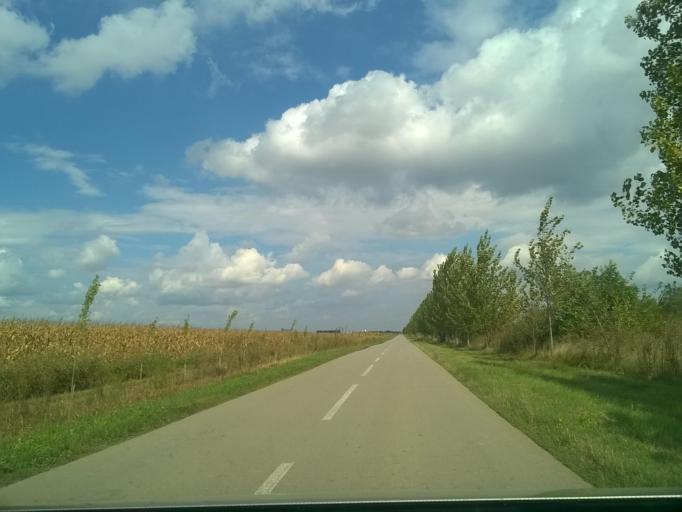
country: RS
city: Debeljaca
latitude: 45.0840
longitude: 20.6033
